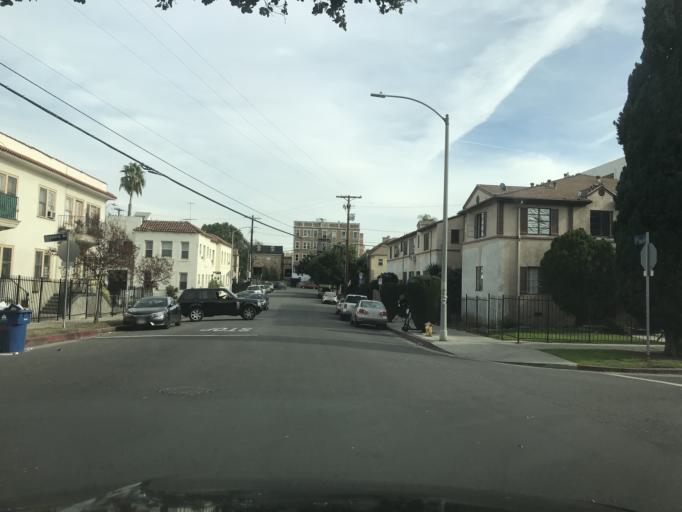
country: US
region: California
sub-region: Los Angeles County
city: Silver Lake
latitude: 34.0712
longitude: -118.2980
